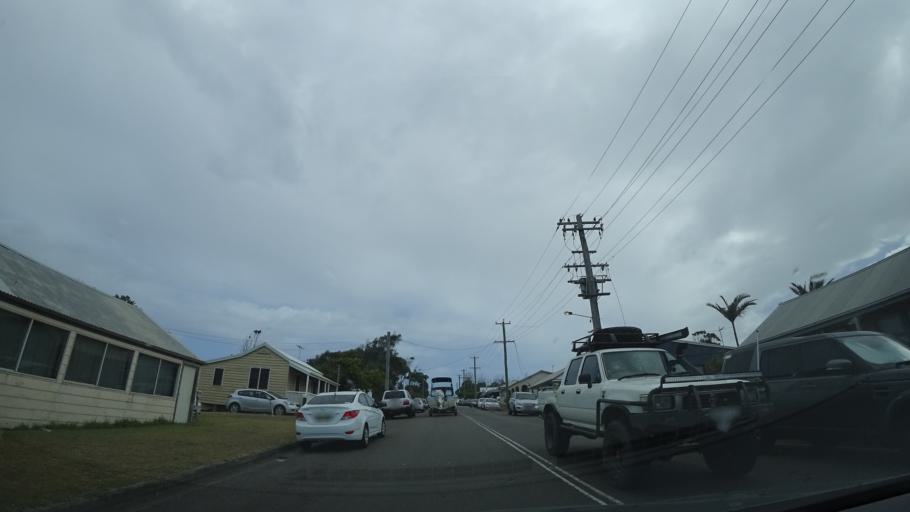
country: AU
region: New South Wales
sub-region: Wyong Shire
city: Kingfisher Shores
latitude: -33.1590
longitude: 151.6271
